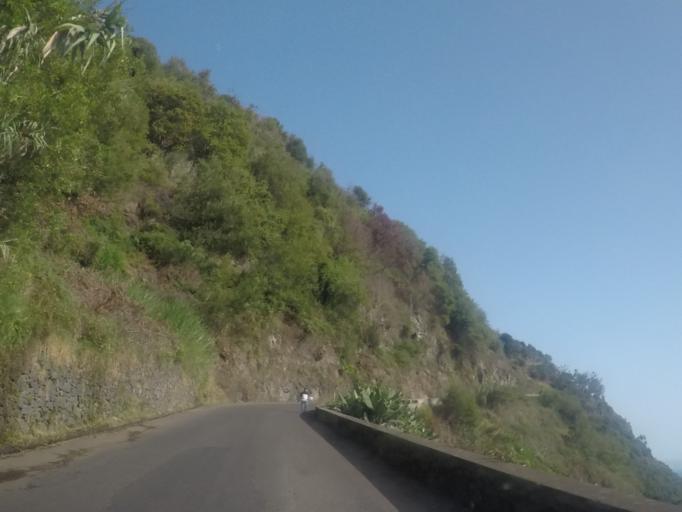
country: PT
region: Madeira
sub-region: Calheta
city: Arco da Calheta
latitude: 32.7124
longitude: -17.1305
